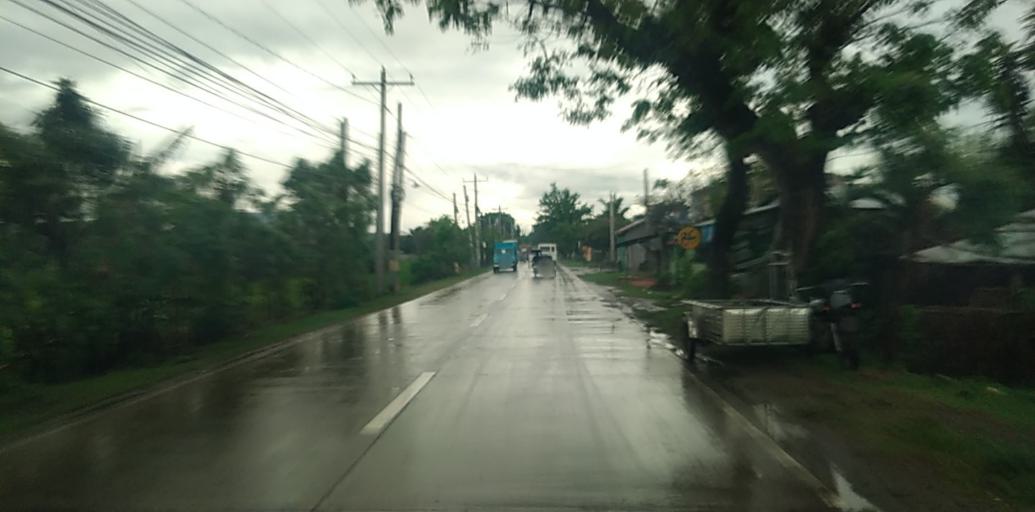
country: PH
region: Central Luzon
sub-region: Province of Pampanga
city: Arayat
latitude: 15.1535
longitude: 120.7303
